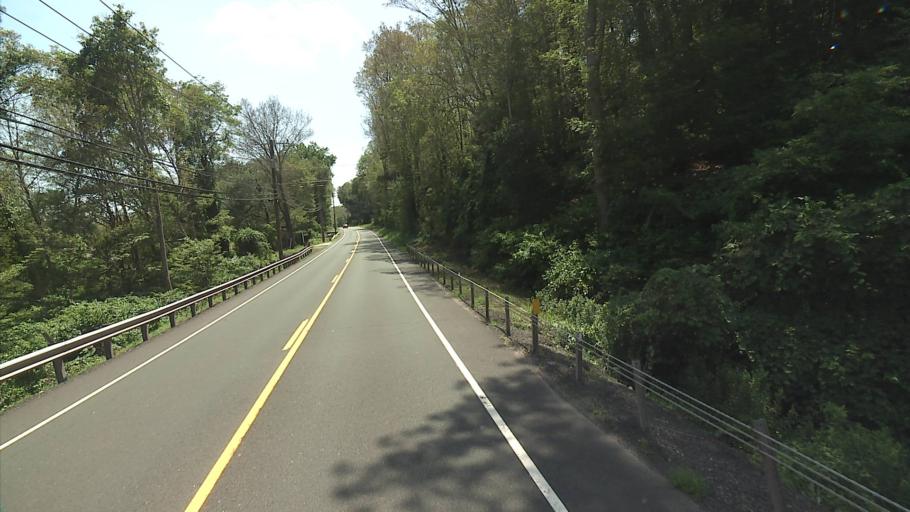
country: US
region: Connecticut
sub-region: Middlesex County
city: East Haddam
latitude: 41.4598
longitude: -72.4796
